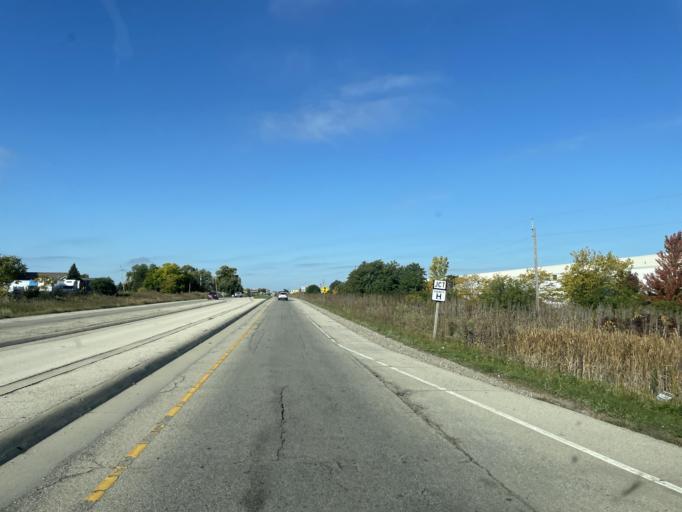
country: US
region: Wisconsin
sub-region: Kenosha County
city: Pleasant Prairie
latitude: 42.5891
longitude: -87.9093
